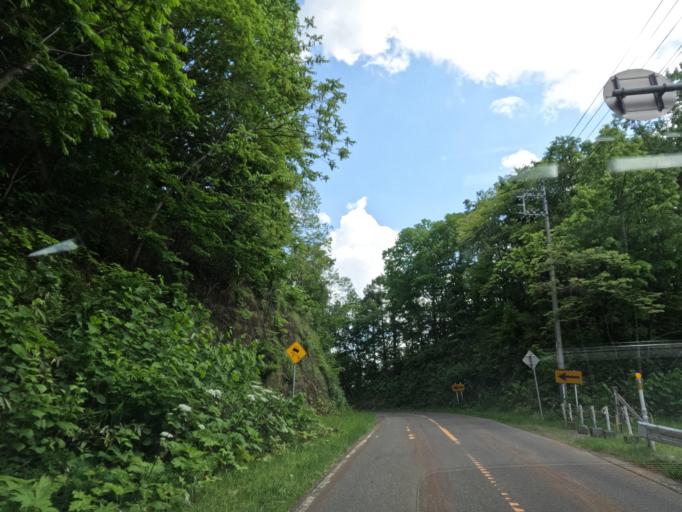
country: JP
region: Hokkaido
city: Takikawa
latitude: 43.5765
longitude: 141.8352
